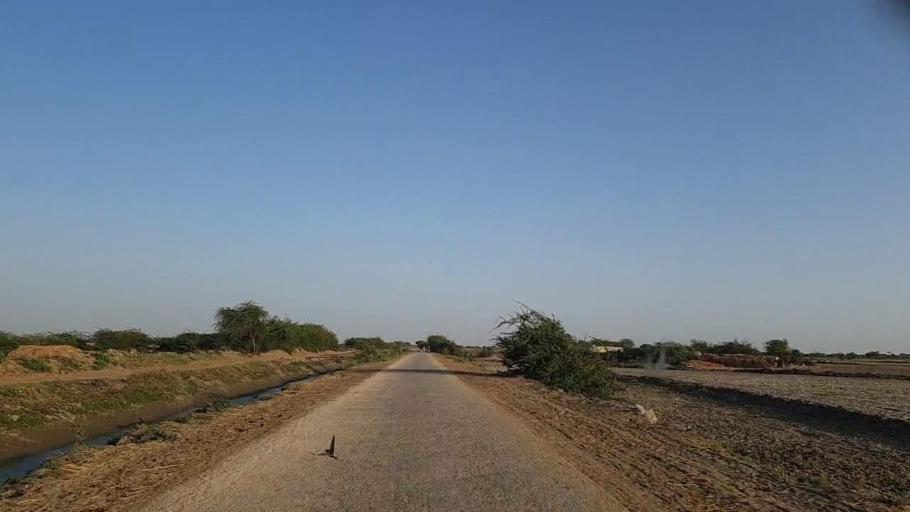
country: PK
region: Sindh
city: Jati
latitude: 24.4142
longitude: 68.3441
